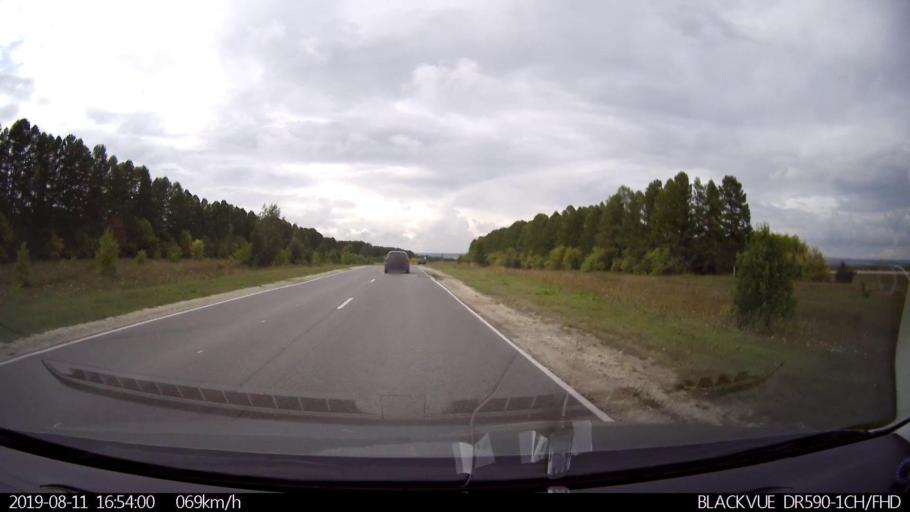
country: RU
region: Ulyanovsk
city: Mayna
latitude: 54.2684
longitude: 47.6678
